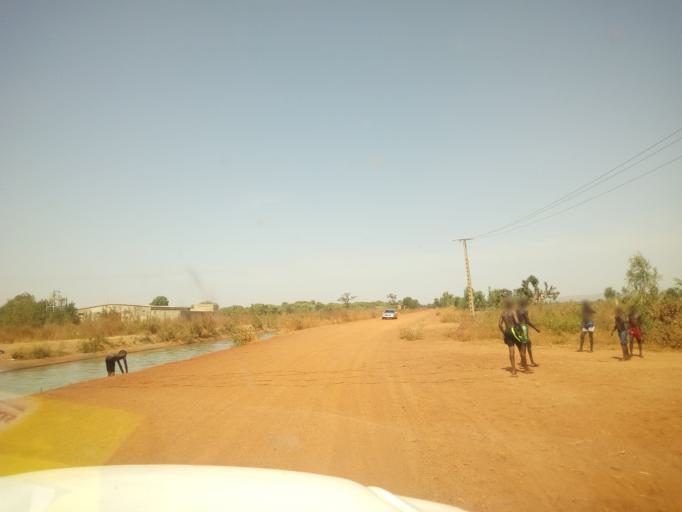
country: ML
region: Bamako
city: Bamako
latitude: 12.6200
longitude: -7.7750
